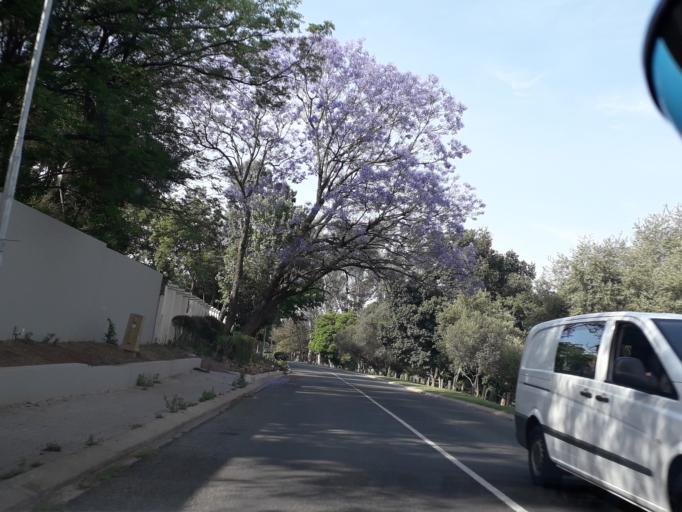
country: ZA
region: Gauteng
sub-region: City of Johannesburg Metropolitan Municipality
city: Midrand
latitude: -26.0674
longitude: 28.0403
